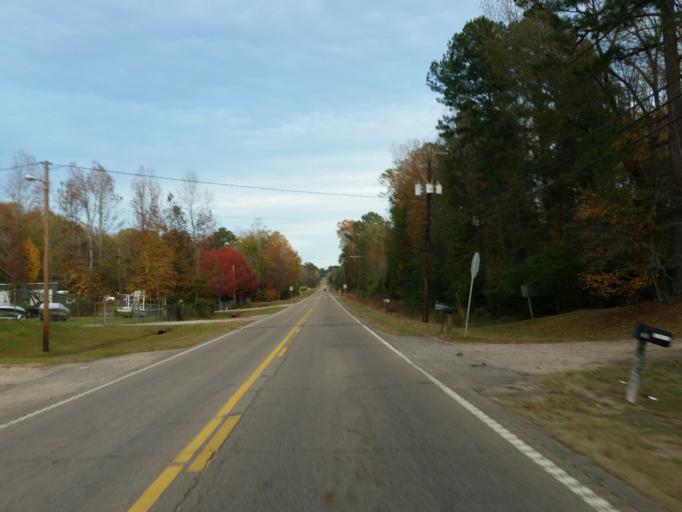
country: US
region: Mississippi
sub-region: Lauderdale County
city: Marion
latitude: 32.4046
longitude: -88.5914
